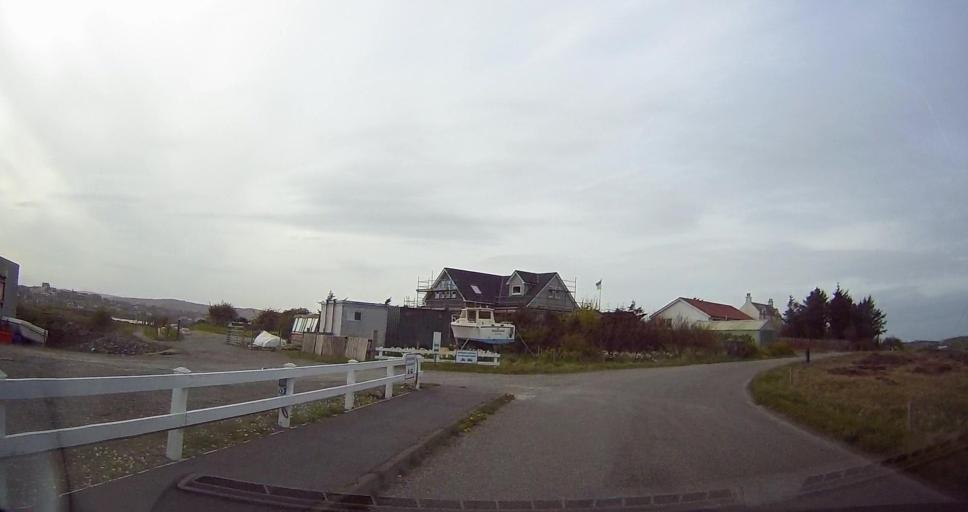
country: GB
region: Scotland
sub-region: Shetland Islands
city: Shetland
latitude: 60.1517
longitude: -1.1148
